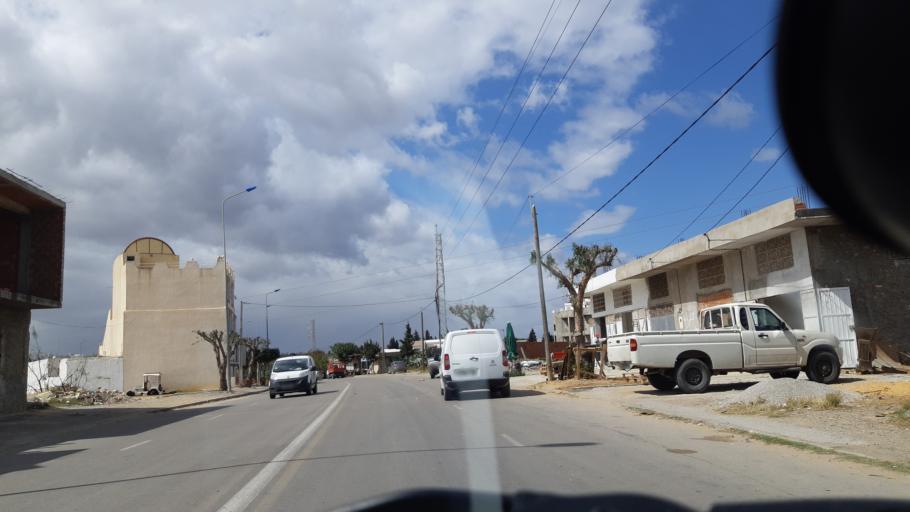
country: TN
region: Susah
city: Akouda
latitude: 35.8795
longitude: 10.5140
